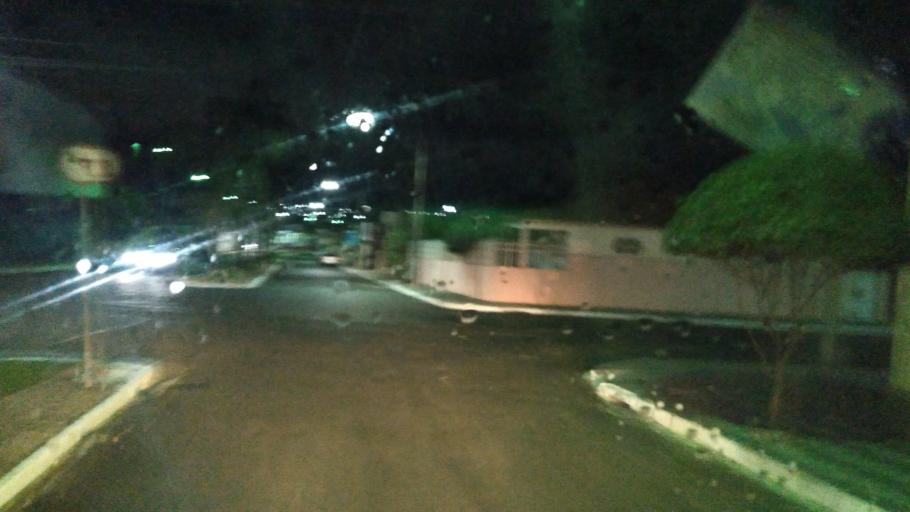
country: BR
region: Goias
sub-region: Mineiros
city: Mineiros
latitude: -17.5651
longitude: -52.5518
